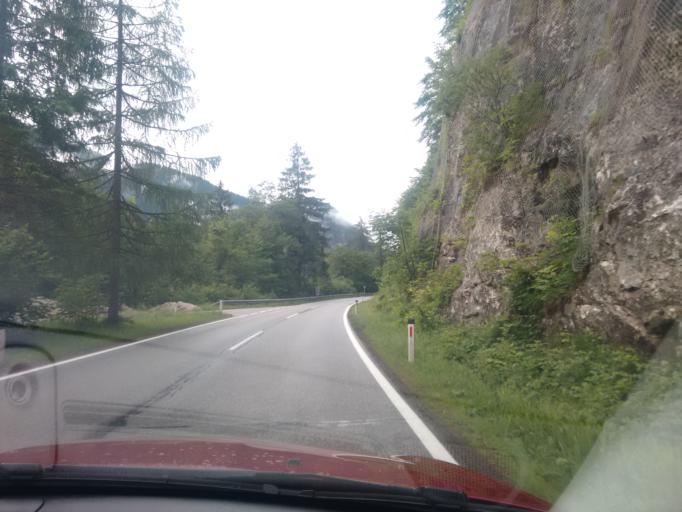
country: AT
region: Upper Austria
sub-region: Politischer Bezirk Gmunden
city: Bad Goisern
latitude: 47.5875
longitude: 13.6571
